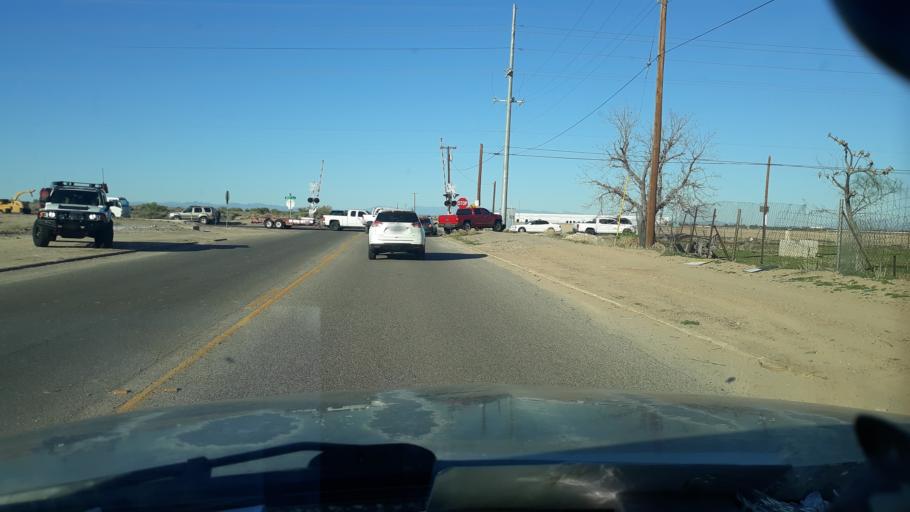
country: US
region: Arizona
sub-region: Maricopa County
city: Citrus Park
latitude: 33.5655
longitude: -112.3936
